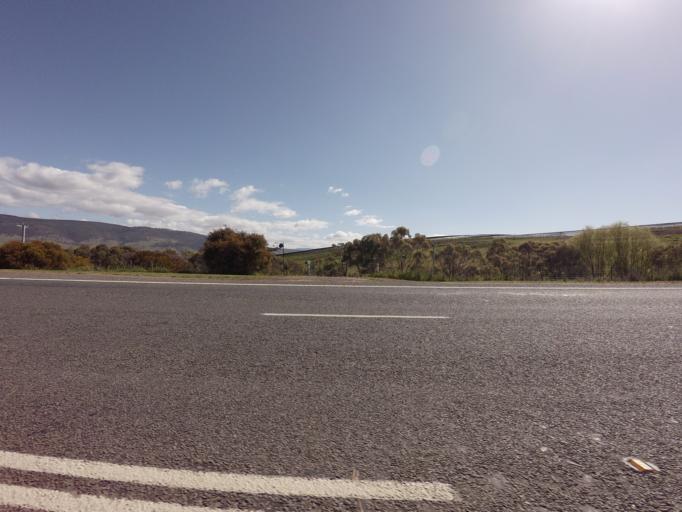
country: AU
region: Tasmania
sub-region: Derwent Valley
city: New Norfolk
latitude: -42.7149
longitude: 146.9464
